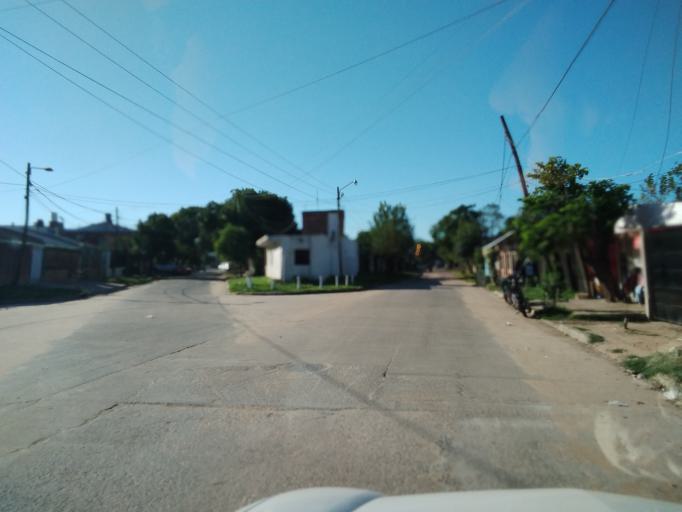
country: AR
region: Corrientes
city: Corrientes
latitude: -27.4710
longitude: -58.7961
